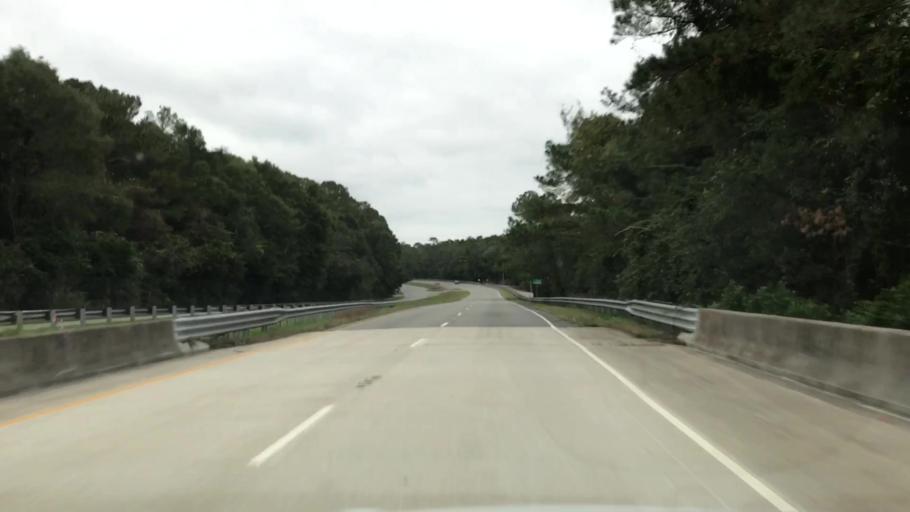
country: US
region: South Carolina
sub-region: Georgetown County
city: Georgetown
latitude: 33.2100
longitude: -79.3834
